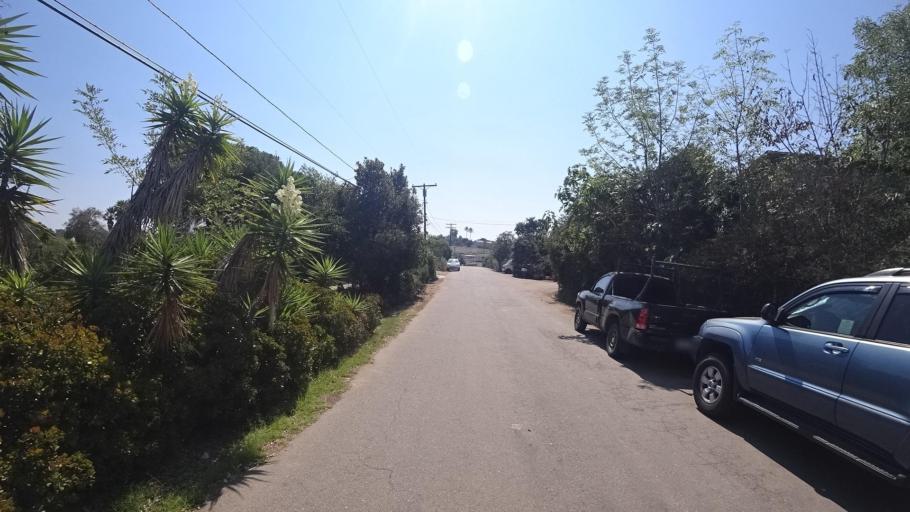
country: US
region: California
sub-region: San Diego County
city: Bonsall
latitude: 33.2501
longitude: -117.2338
